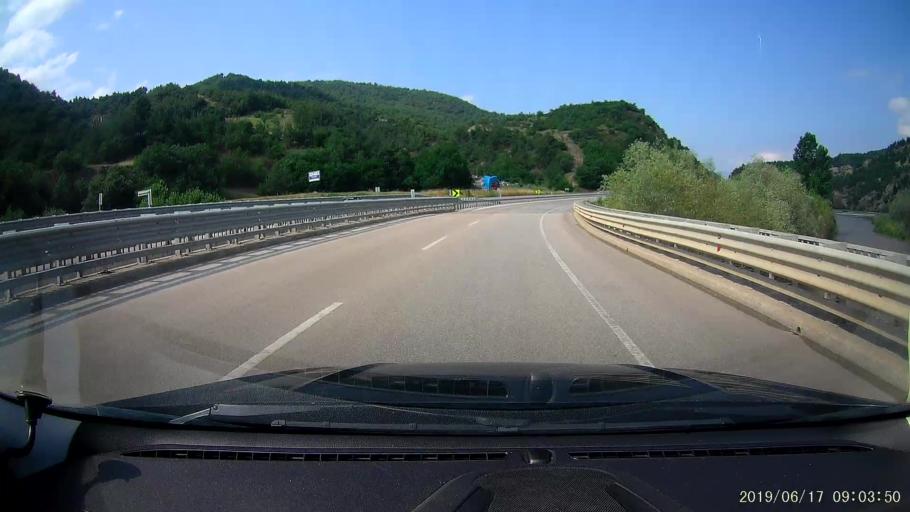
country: TR
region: Amasya
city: Tasova
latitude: 40.7500
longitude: 36.3011
